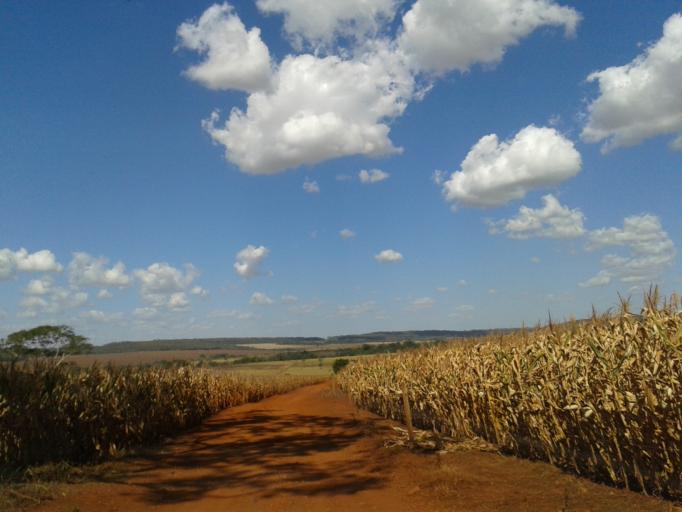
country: BR
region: Minas Gerais
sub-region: Capinopolis
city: Capinopolis
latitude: -18.6223
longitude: -49.4736
